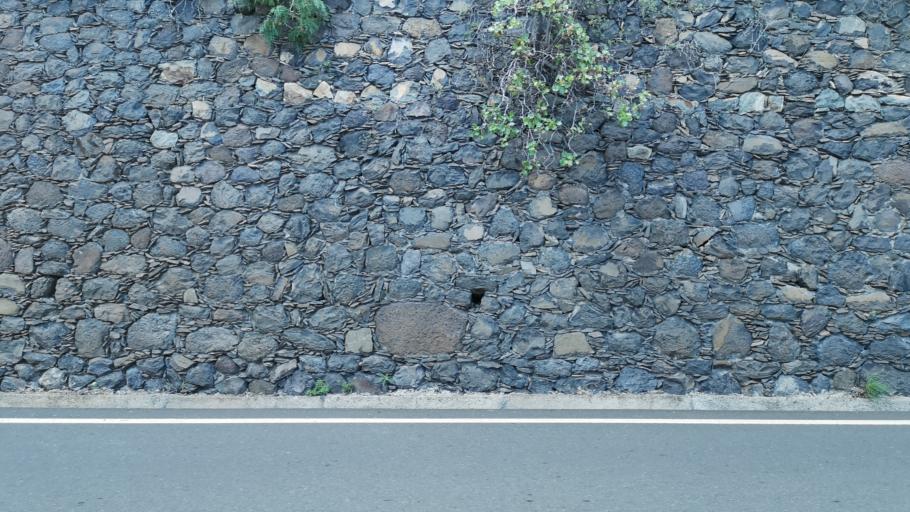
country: ES
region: Canary Islands
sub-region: Provincia de Santa Cruz de Tenerife
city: Agulo
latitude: 28.1852
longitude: -17.1910
